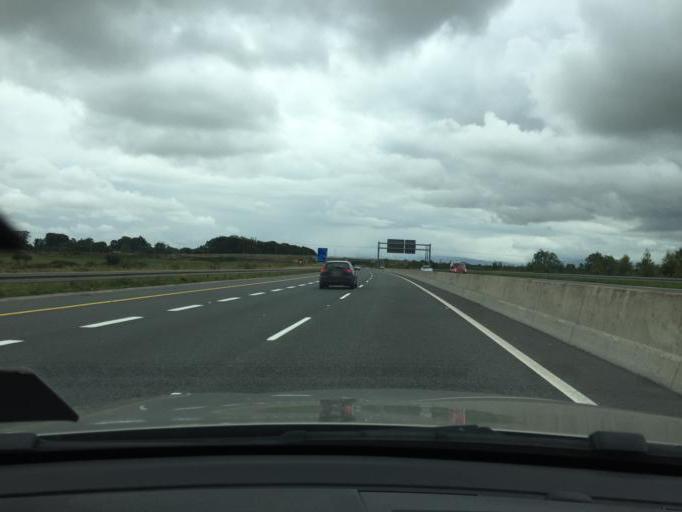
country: IE
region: Leinster
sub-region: An Mhi
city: Dunboyne
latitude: 53.4272
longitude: -6.4629
